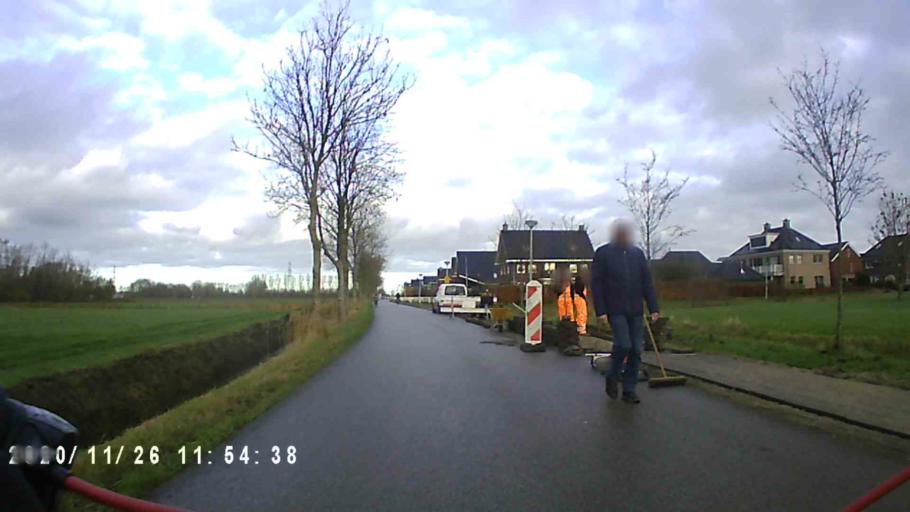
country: NL
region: Groningen
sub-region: Gemeente Bedum
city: Bedum
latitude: 53.3050
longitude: 6.6050
